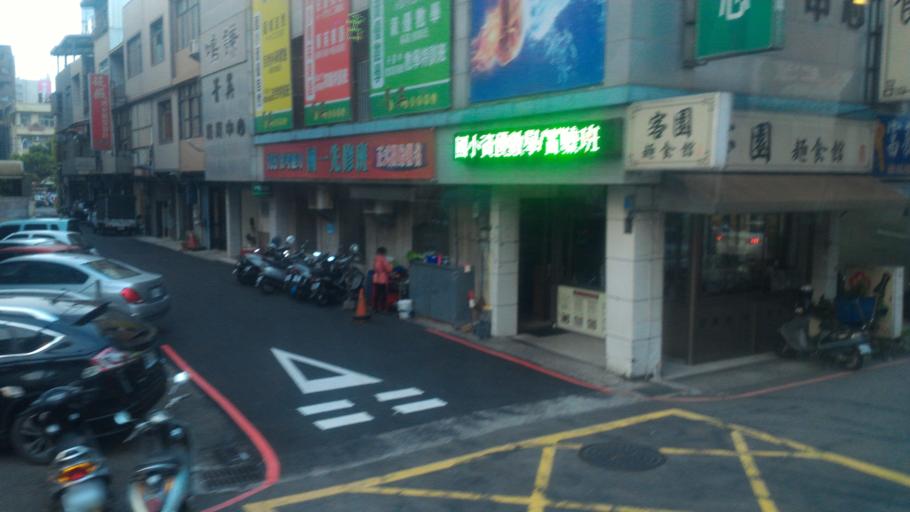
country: TW
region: Taiwan
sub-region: Hsinchu
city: Hsinchu
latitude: 24.8082
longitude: 120.9779
